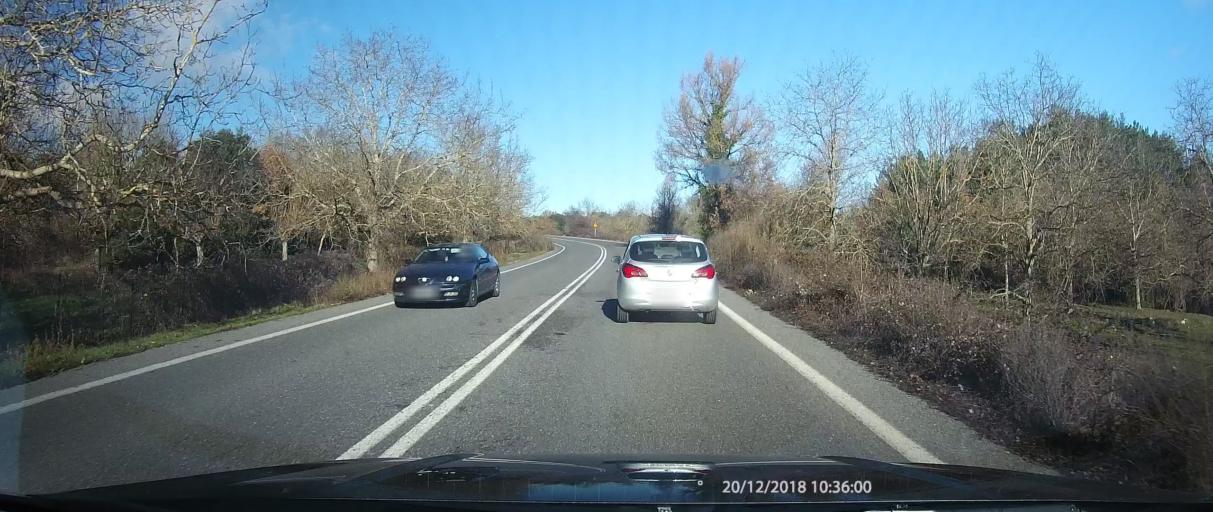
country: GR
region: Peloponnese
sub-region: Nomos Lakonias
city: Kariai
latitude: 37.3611
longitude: 22.4048
